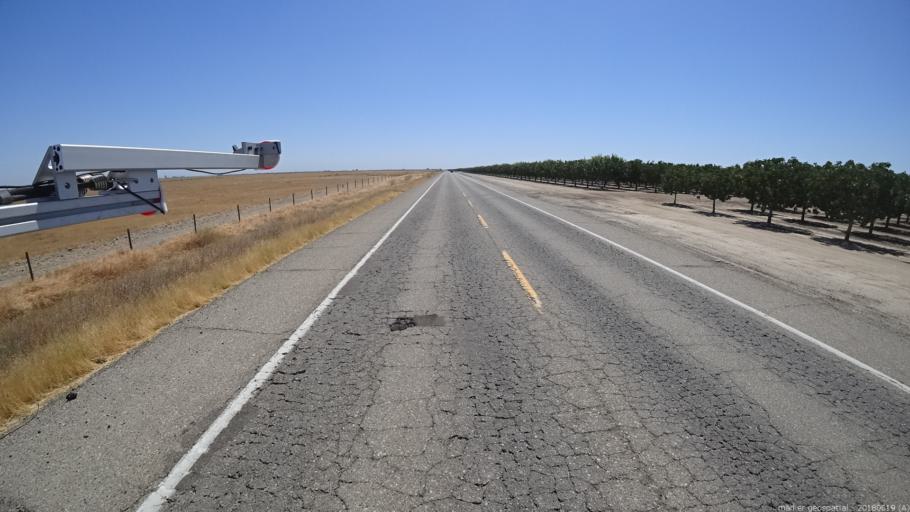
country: US
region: California
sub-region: Fresno County
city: Mendota
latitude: 36.8510
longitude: -120.2465
